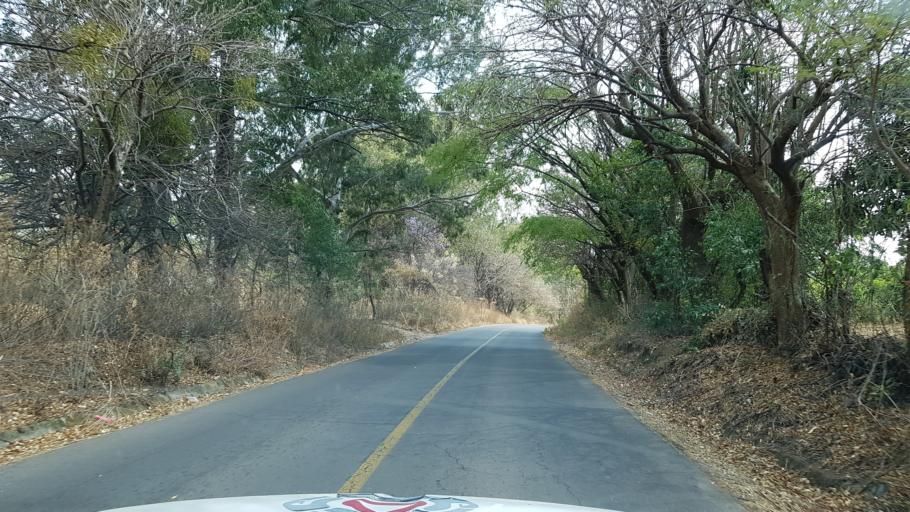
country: MX
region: Morelos
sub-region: Yecapixtla
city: Texcala
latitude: 18.9074
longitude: -98.8078
